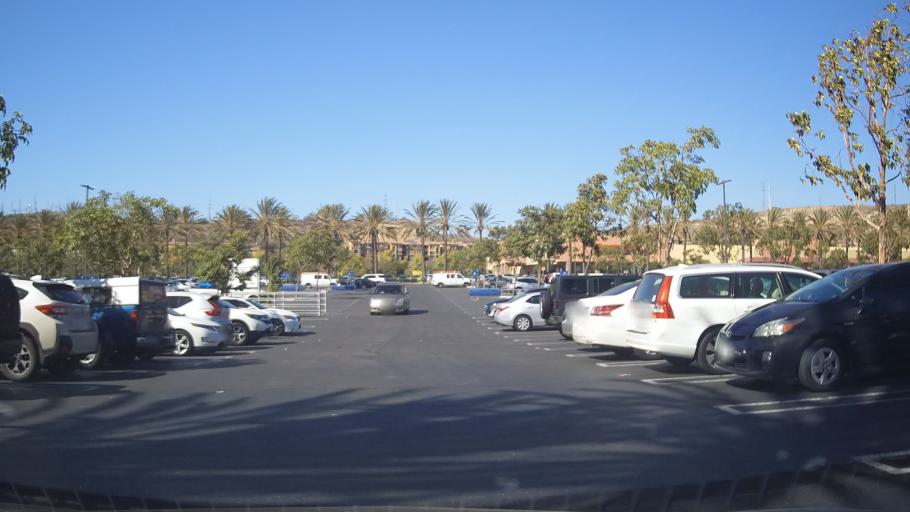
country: US
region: California
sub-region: San Diego County
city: San Diego
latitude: 32.7802
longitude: -117.1276
